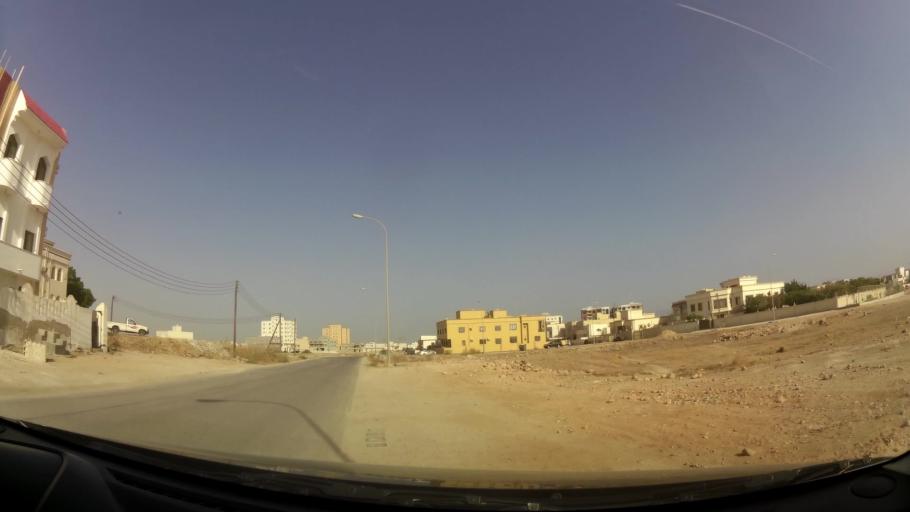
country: OM
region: Zufar
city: Salalah
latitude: 17.0124
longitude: 54.0187
